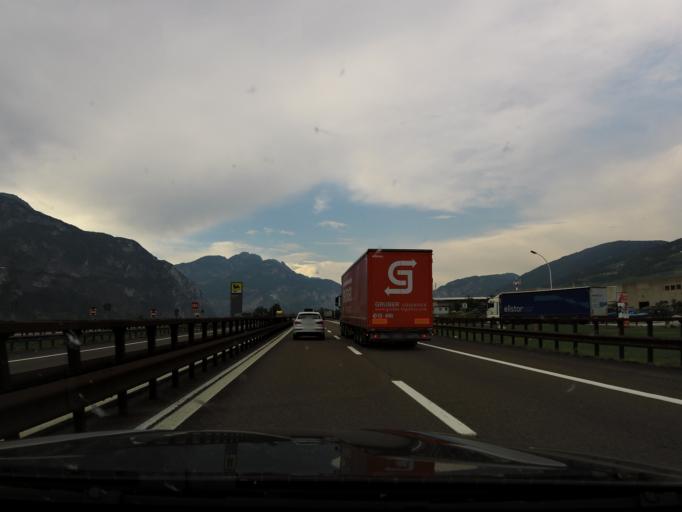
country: IT
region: Trentino-Alto Adige
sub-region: Provincia di Trento
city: Zambana
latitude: 46.1421
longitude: 11.0871
